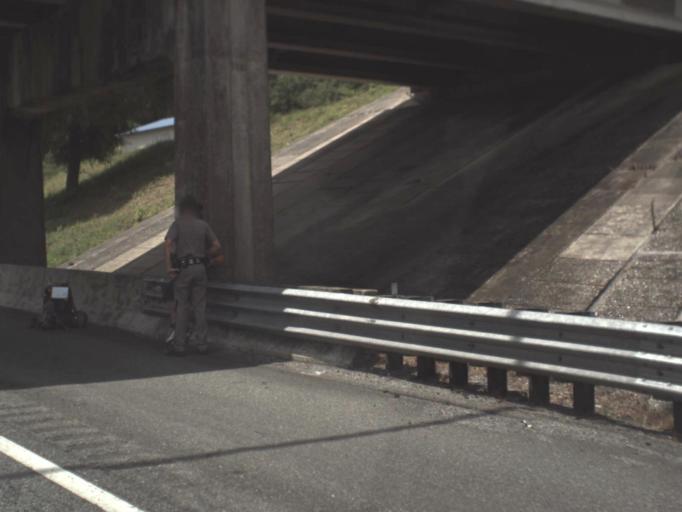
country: US
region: Florida
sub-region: Suwannee County
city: Wellborn
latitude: 30.2613
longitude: -82.7515
